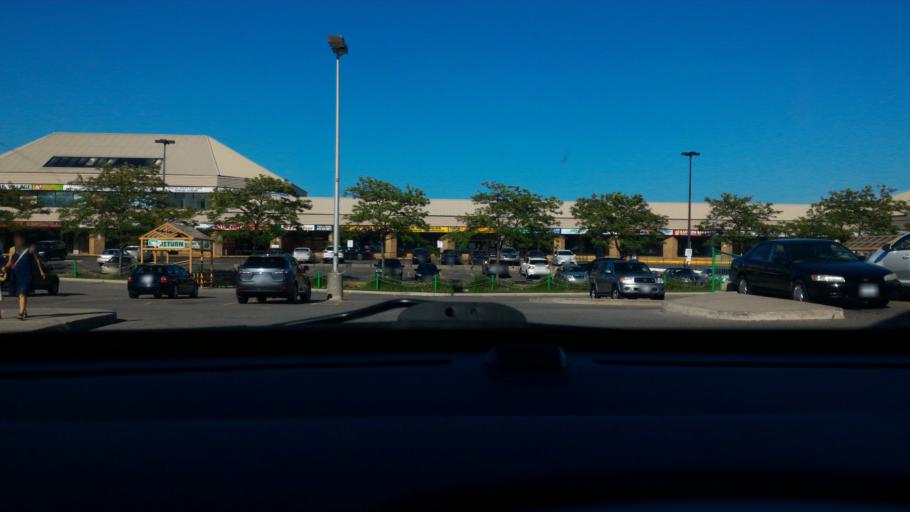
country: CA
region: Ontario
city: Scarborough
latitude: 43.7664
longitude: -79.2833
